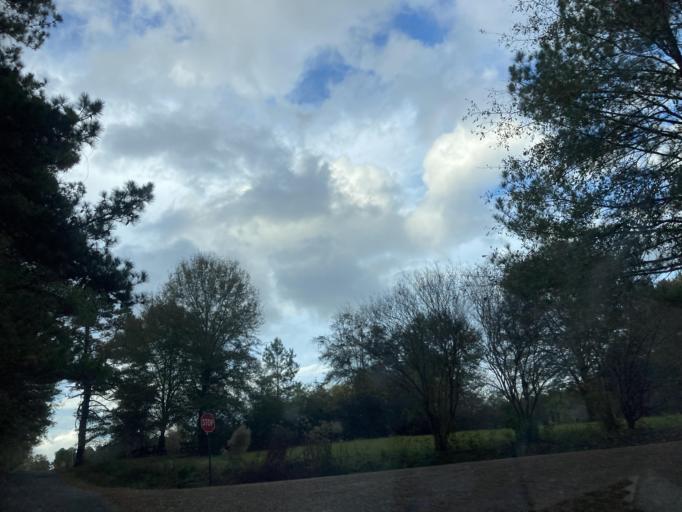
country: US
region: Mississippi
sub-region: Marion County
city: Columbia
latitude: 31.1931
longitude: -89.6454
